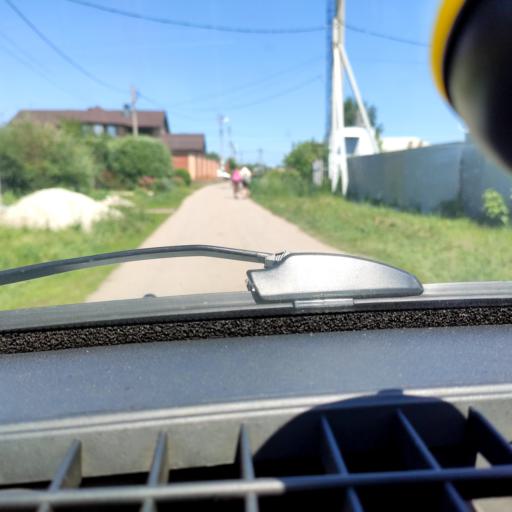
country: RU
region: Samara
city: Podstepki
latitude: 53.5112
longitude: 49.2294
